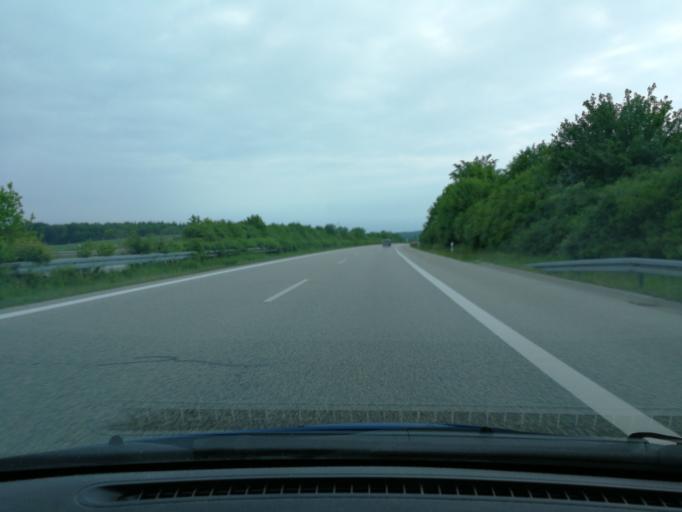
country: DE
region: Mecklenburg-Vorpommern
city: Bobitz
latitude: 53.8297
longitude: 11.3625
